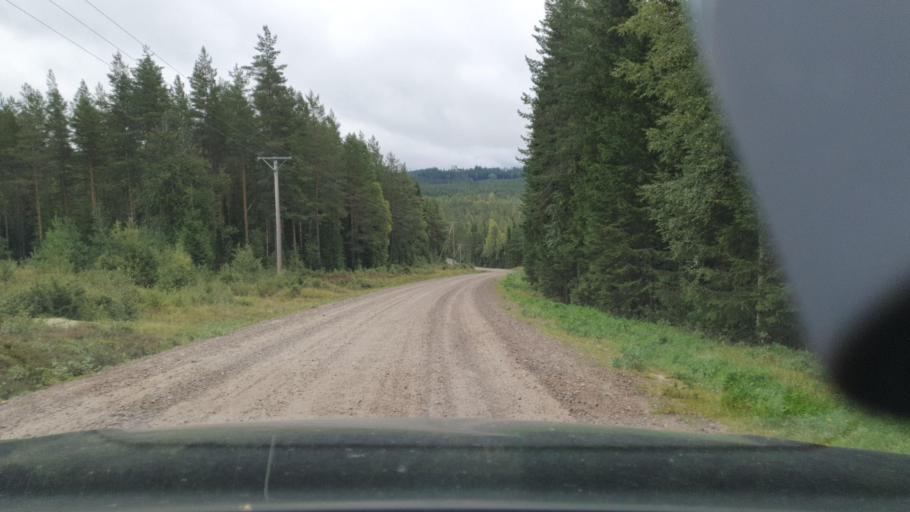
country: SE
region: Vaermland
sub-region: Torsby Kommun
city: Torsby
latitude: 60.4745
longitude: 12.8939
